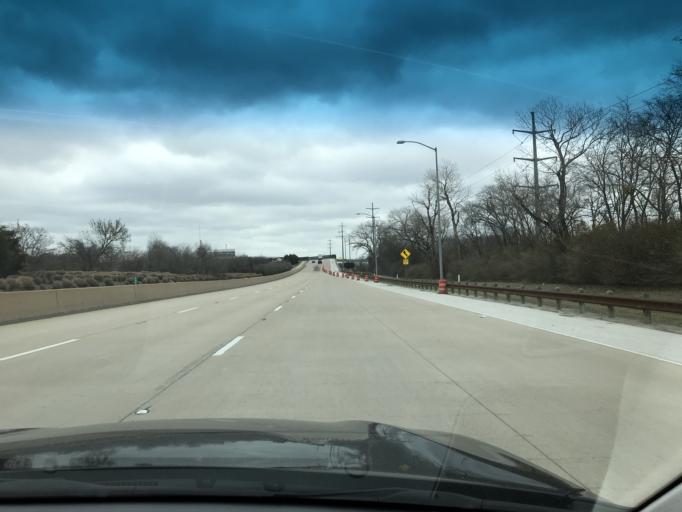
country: US
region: Texas
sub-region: Tarrant County
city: Westworth
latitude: 32.7150
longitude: -97.3925
